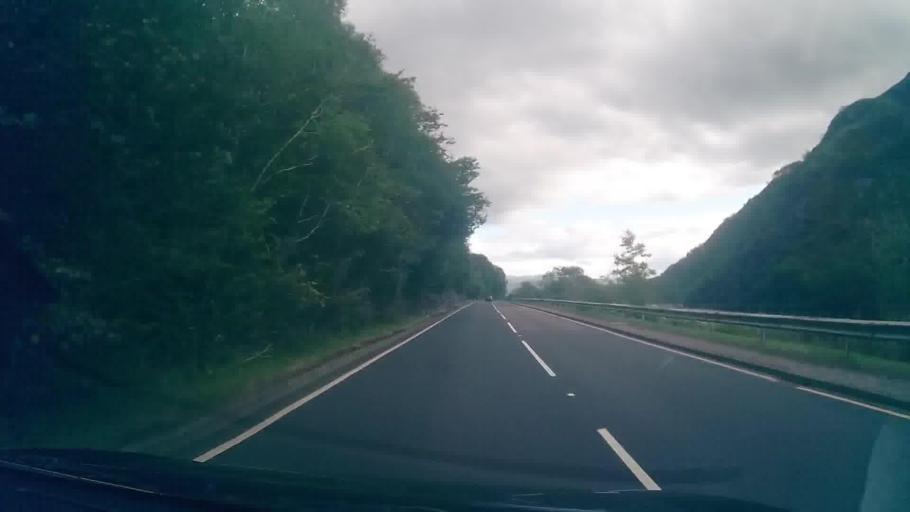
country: GB
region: Scotland
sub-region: Argyll and Bute
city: Oban
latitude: 56.3974
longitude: -5.1315
